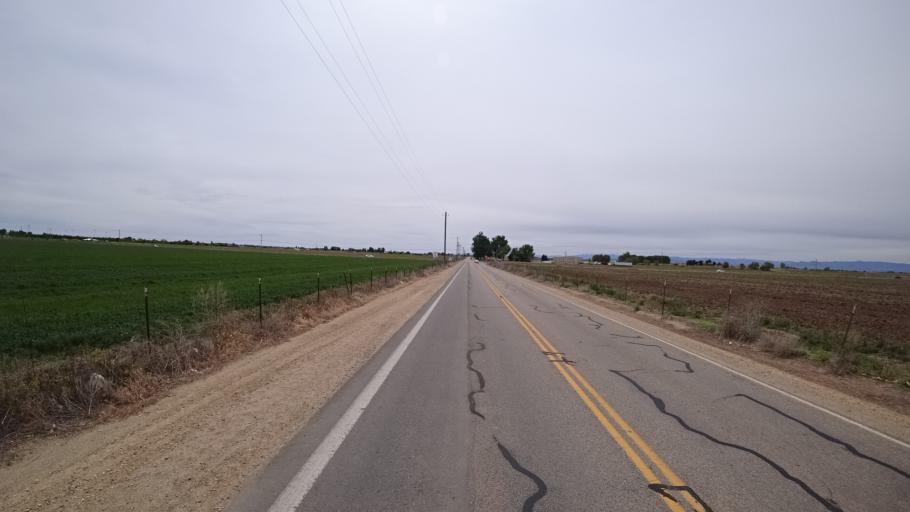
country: US
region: Idaho
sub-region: Ada County
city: Meridian
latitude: 43.5480
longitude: -116.3745
